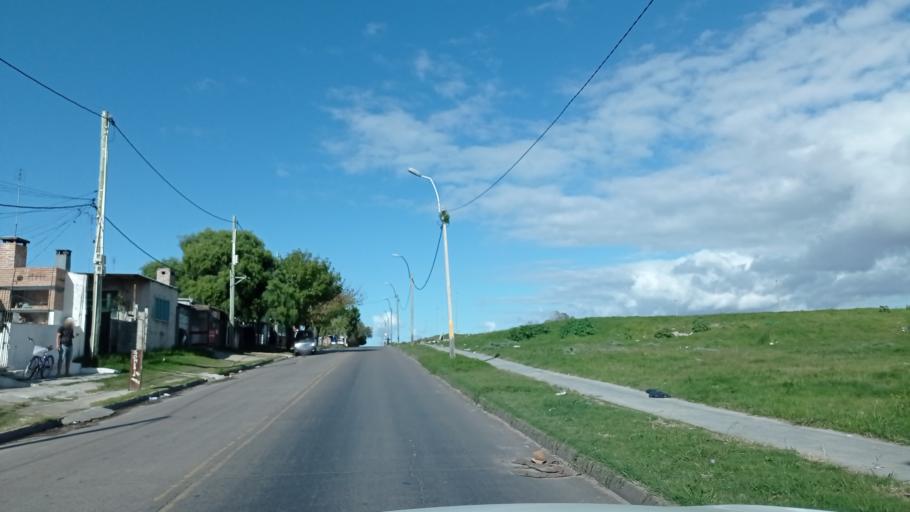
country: UY
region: Canelones
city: Paso de Carrasco
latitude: -34.8781
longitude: -56.1183
